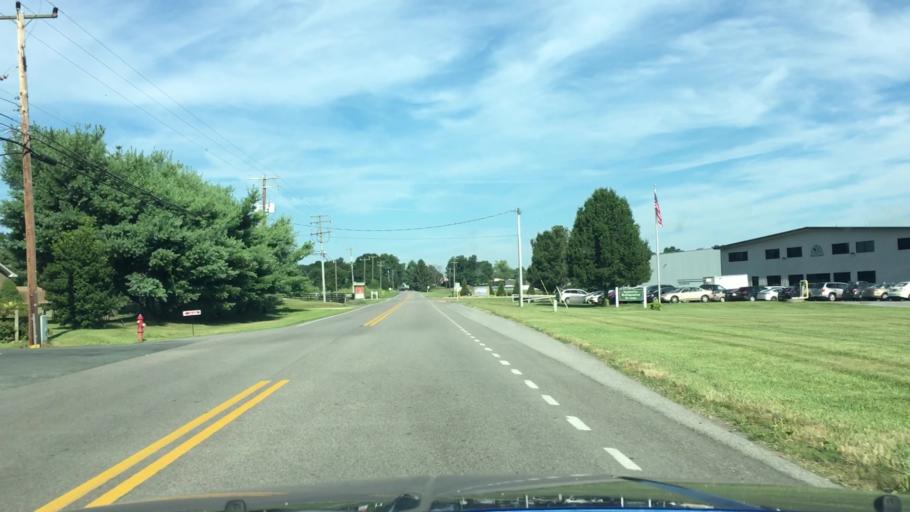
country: US
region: Virginia
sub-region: Augusta County
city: Lyndhurst
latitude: 38.0287
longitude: -78.9368
